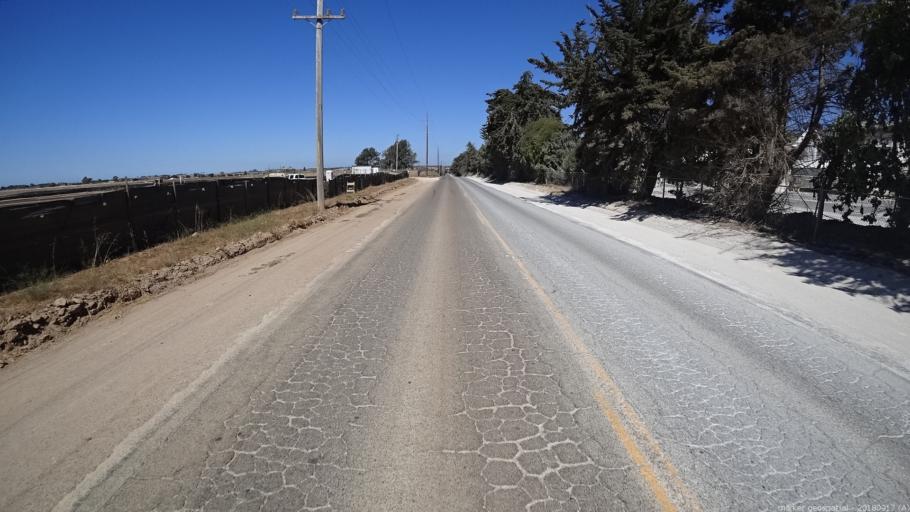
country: US
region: California
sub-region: Monterey County
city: Prunedale
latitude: 36.7471
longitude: -121.6054
